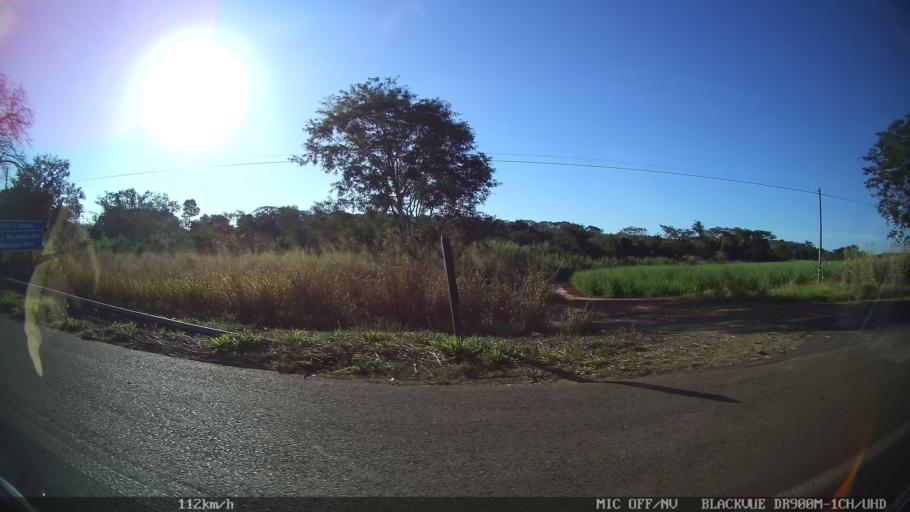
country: BR
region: Sao Paulo
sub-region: Guapiacu
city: Guapiacu
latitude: -20.7422
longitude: -49.1022
